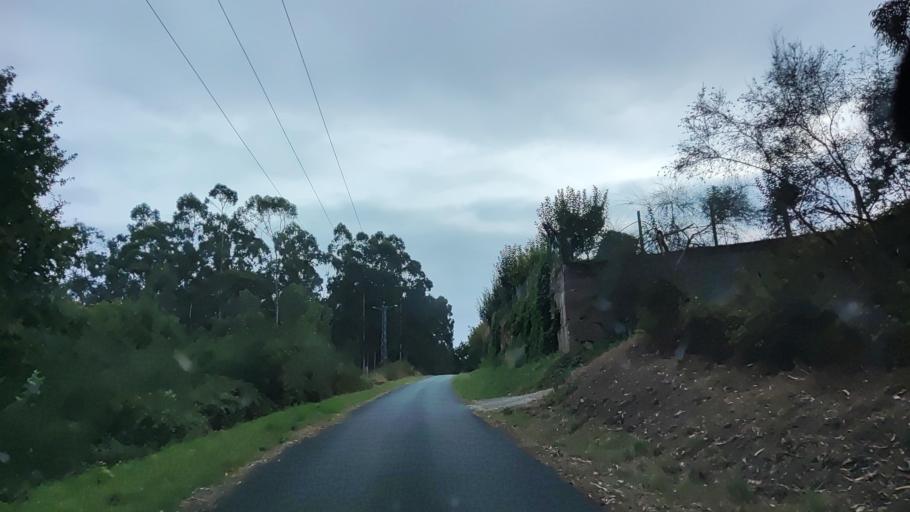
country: ES
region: Galicia
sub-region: Provincia da Coruna
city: Padron
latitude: 42.7209
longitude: -8.6792
